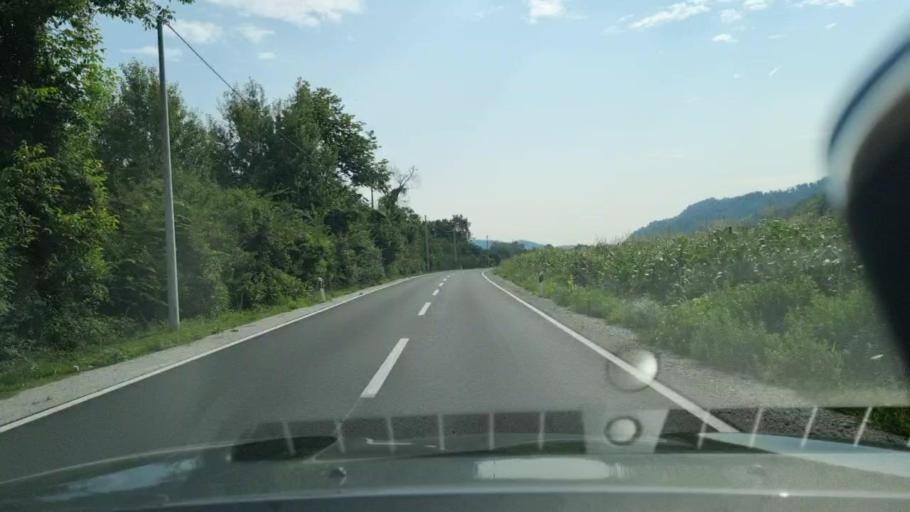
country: BA
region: Federation of Bosnia and Herzegovina
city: Otoka
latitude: 44.9804
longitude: 16.1892
